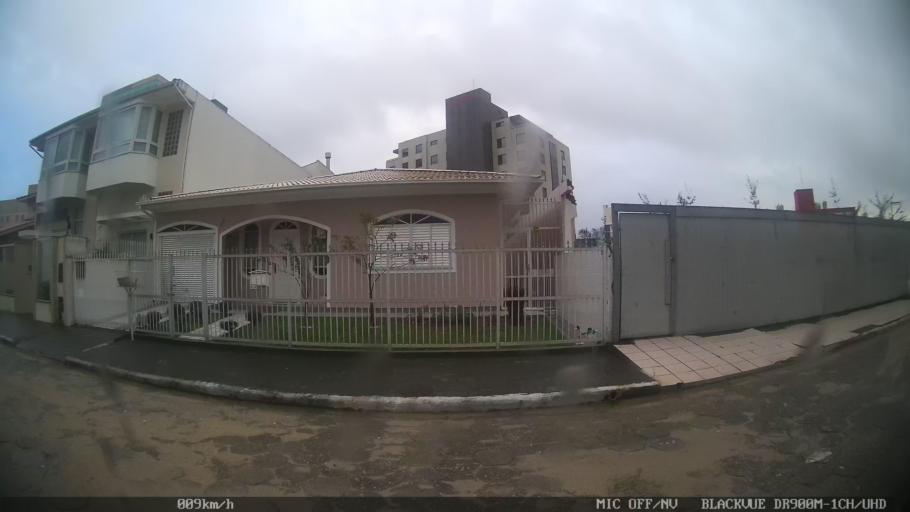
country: BR
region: Santa Catarina
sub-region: Sao Jose
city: Campinas
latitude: -27.5980
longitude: -48.6180
